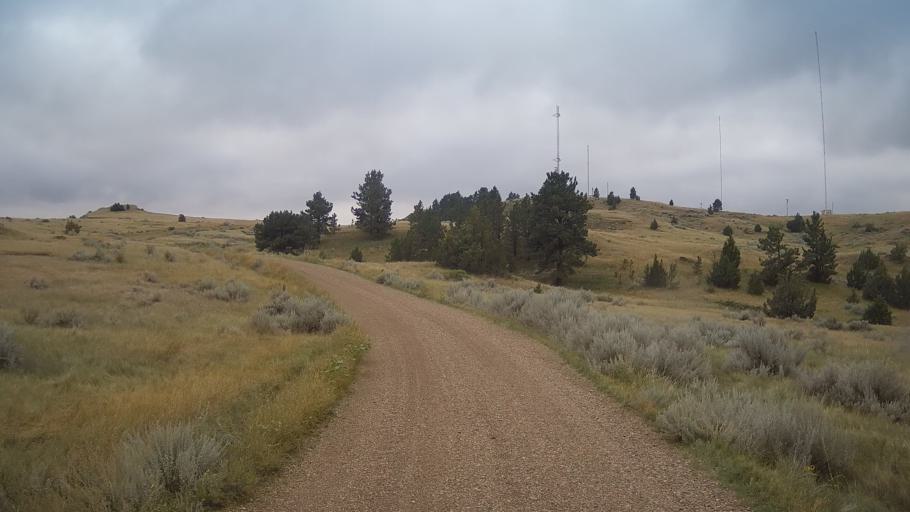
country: US
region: Montana
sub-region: Dawson County
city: Glendive
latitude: 47.0562
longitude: -104.6715
